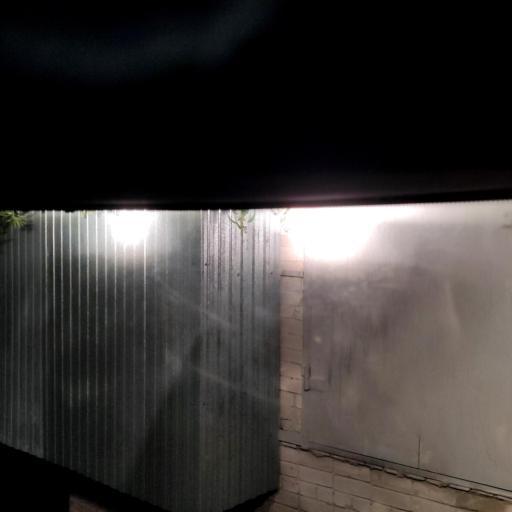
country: RU
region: Samara
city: Petra-Dubrava
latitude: 53.3125
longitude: 50.2817
